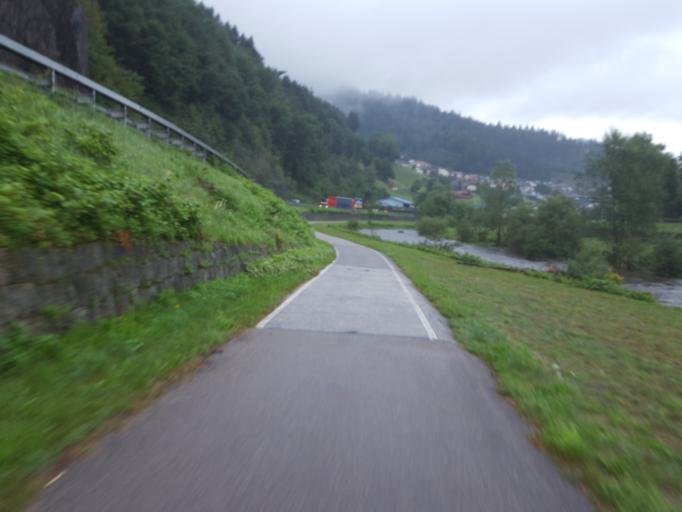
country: DE
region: Baden-Wuerttemberg
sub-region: Freiburg Region
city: Wolfach
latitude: 48.2846
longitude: 8.2116
